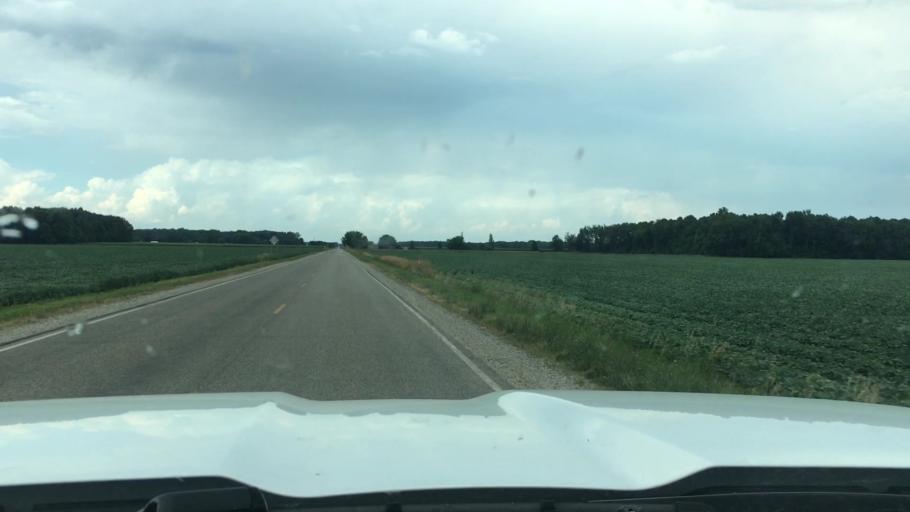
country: US
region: Michigan
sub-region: Montcalm County
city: Carson City
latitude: 43.1776
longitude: -84.7781
